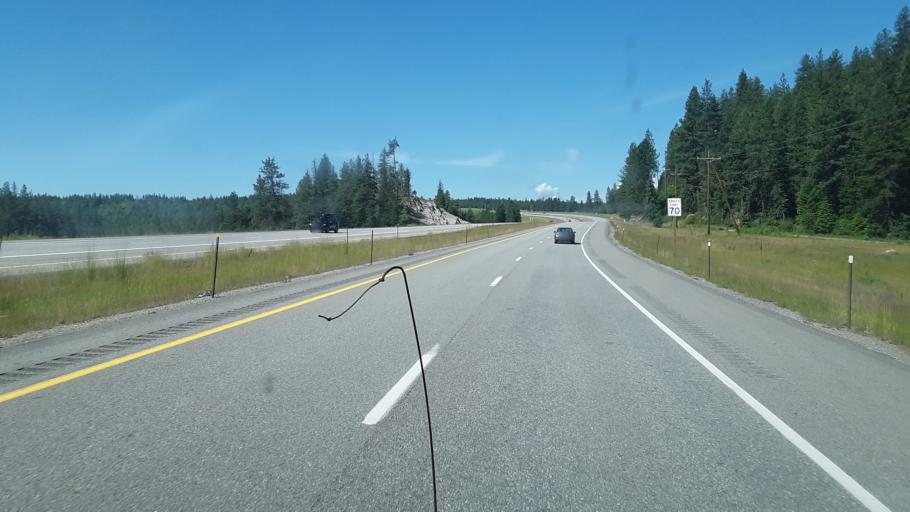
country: US
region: Idaho
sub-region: Kootenai County
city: Spirit Lake
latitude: 47.9919
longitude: -116.6835
